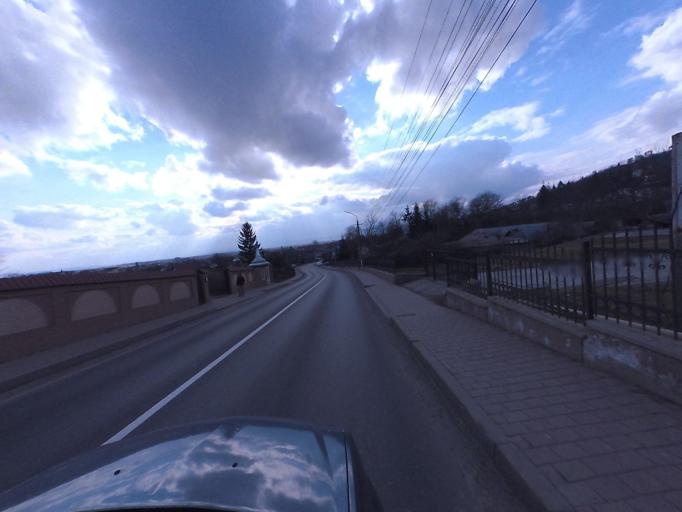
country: RO
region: Neamt
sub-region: Oras Targu Neamt
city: Targu Neamt
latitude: 47.2107
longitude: 26.3761
